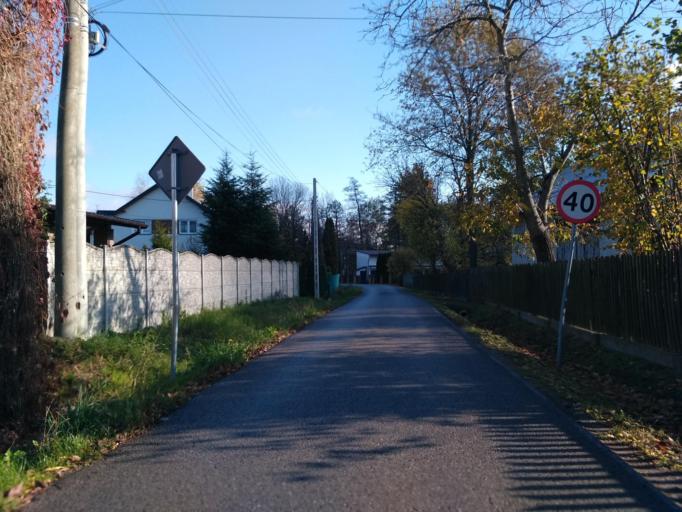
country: PL
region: Subcarpathian Voivodeship
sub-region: Powiat rzeszowski
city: Niechobrz
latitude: 49.9970
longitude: 21.8808
